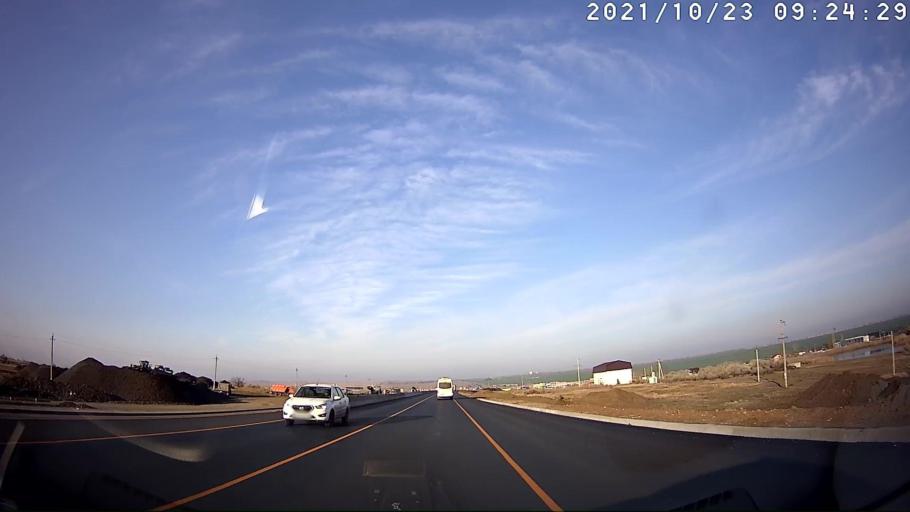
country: RU
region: Saratov
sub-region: Saratovskiy Rayon
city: Saratov
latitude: 51.6703
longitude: 45.9885
